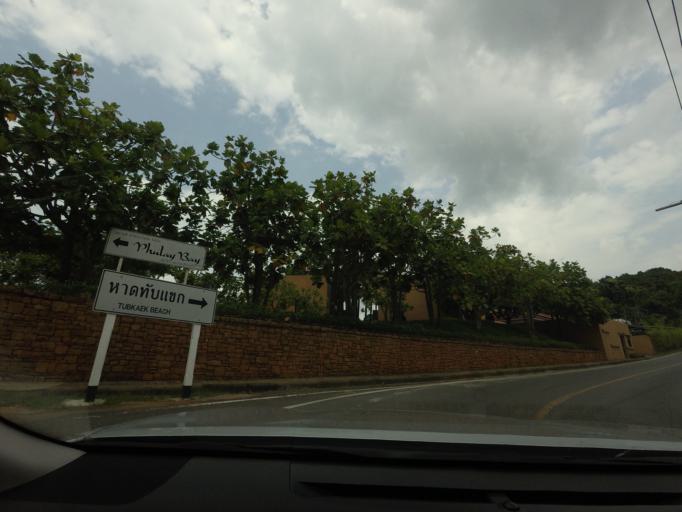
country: TH
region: Phangnga
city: Ban Ao Nang
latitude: 8.0840
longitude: 98.7457
